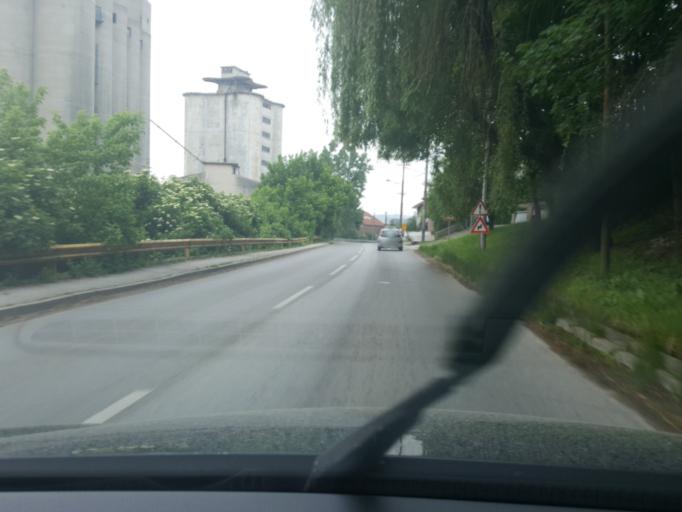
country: RS
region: Central Serbia
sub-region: Kolubarski Okrug
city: Valjevo
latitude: 44.2659
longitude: 19.8785
